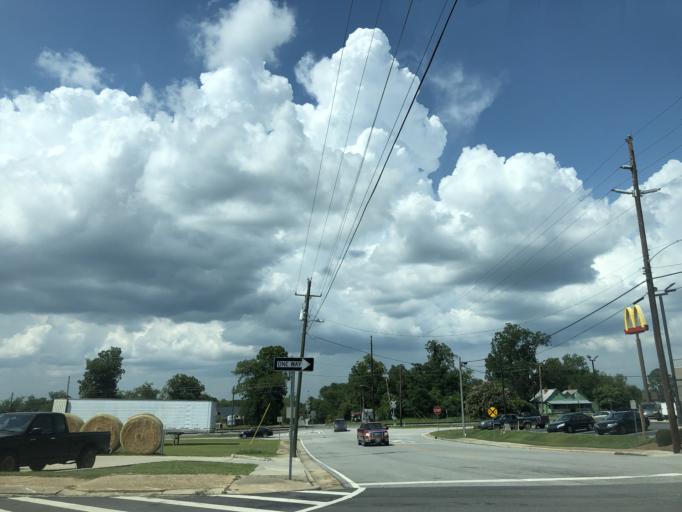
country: US
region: Georgia
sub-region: Telfair County
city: McRae
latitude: 32.0674
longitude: -82.8984
